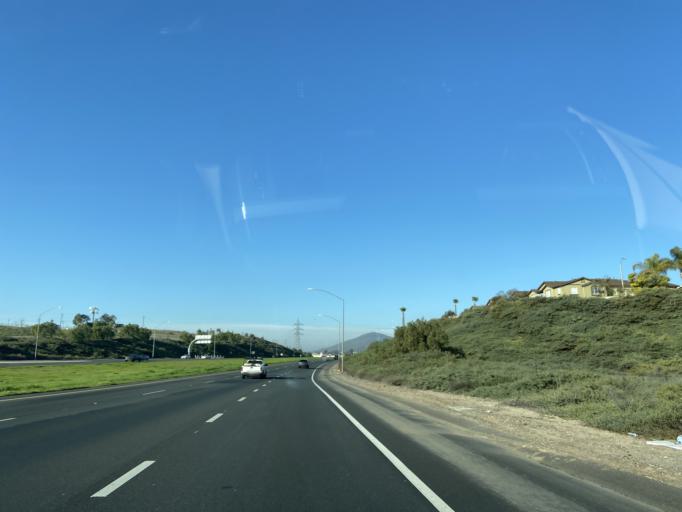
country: US
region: California
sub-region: San Diego County
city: Bonita
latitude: 32.6350
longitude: -116.9711
